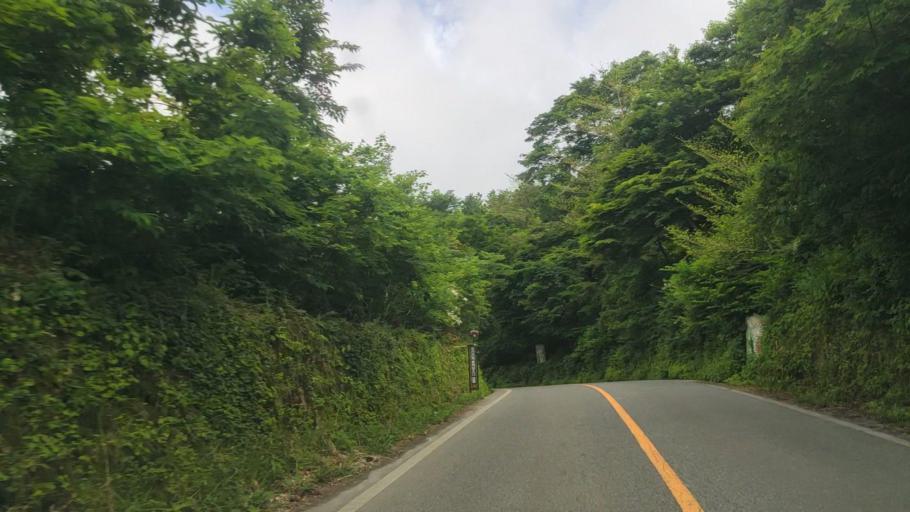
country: JP
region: Tottori
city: Yonago
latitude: 35.3583
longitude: 133.5310
